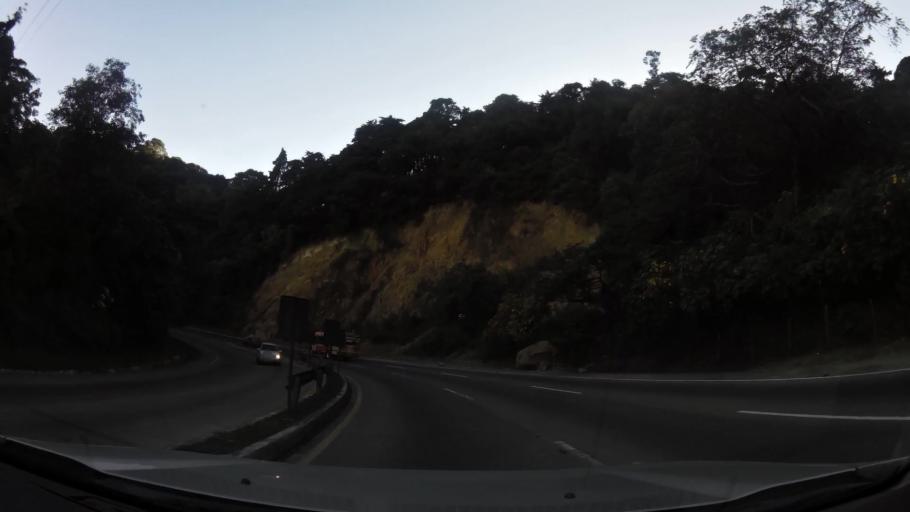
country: GT
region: Guatemala
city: Mixco
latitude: 14.6100
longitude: -90.6258
